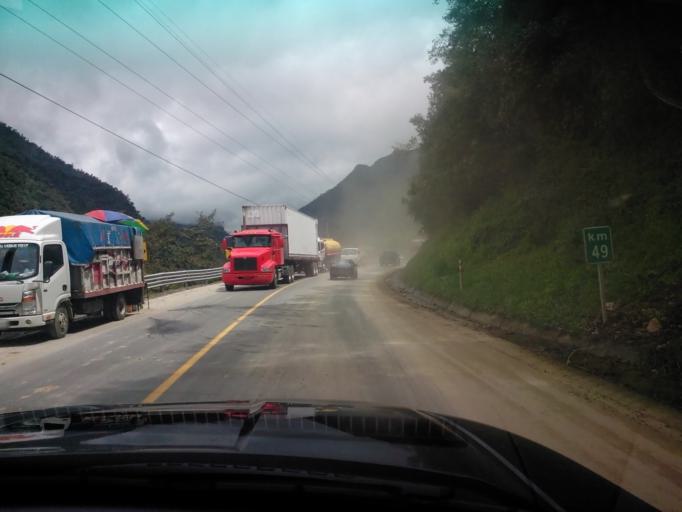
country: EC
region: Pichincha
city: Sangolqui
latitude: -0.3696
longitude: -78.1031
